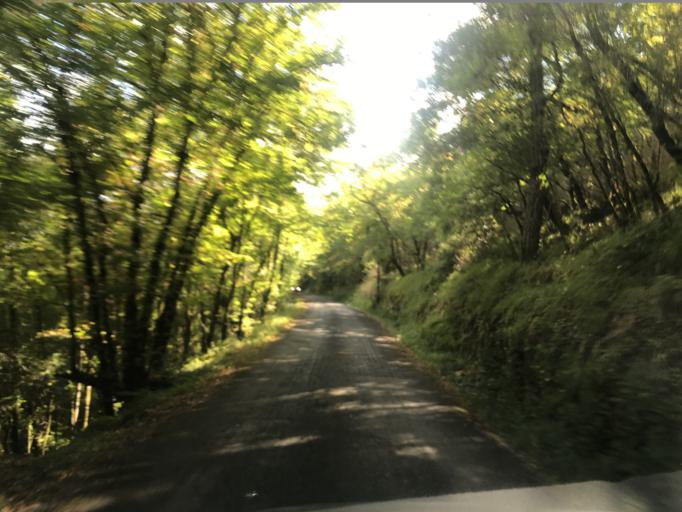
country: FR
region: Aquitaine
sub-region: Departement de la Dordogne
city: Rouffignac-Saint-Cernin-de-Reilhac
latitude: 44.9735
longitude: 1.0328
